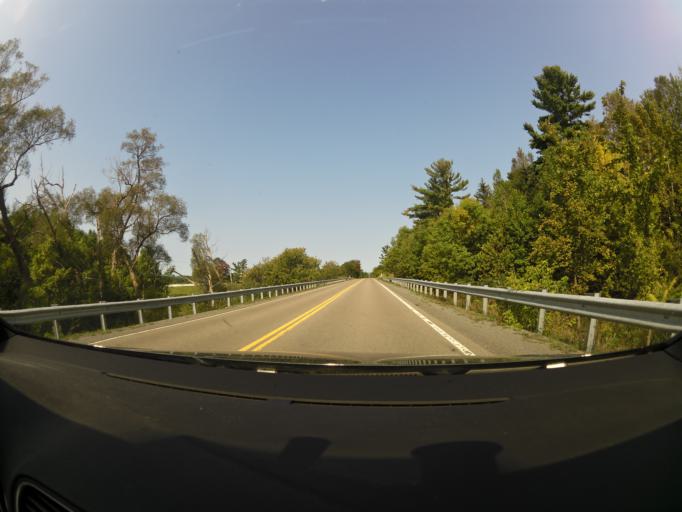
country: CA
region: Ontario
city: Arnprior
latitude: 45.4405
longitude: -76.1804
